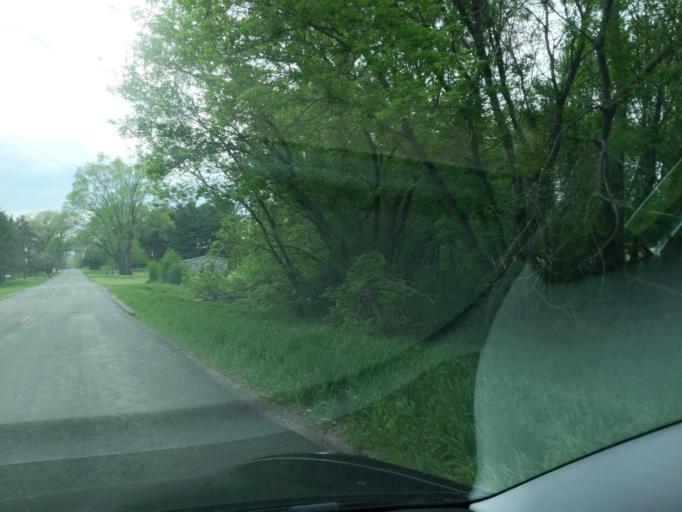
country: US
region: Michigan
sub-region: Ingham County
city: Stockbridge
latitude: 42.4393
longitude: -84.1635
